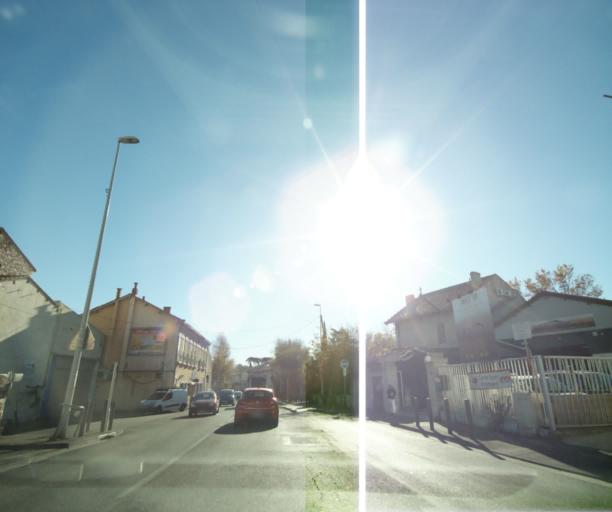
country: FR
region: Provence-Alpes-Cote d'Azur
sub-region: Departement des Bouches-du-Rhone
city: Marseille 15
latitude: 43.3755
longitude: 5.3559
